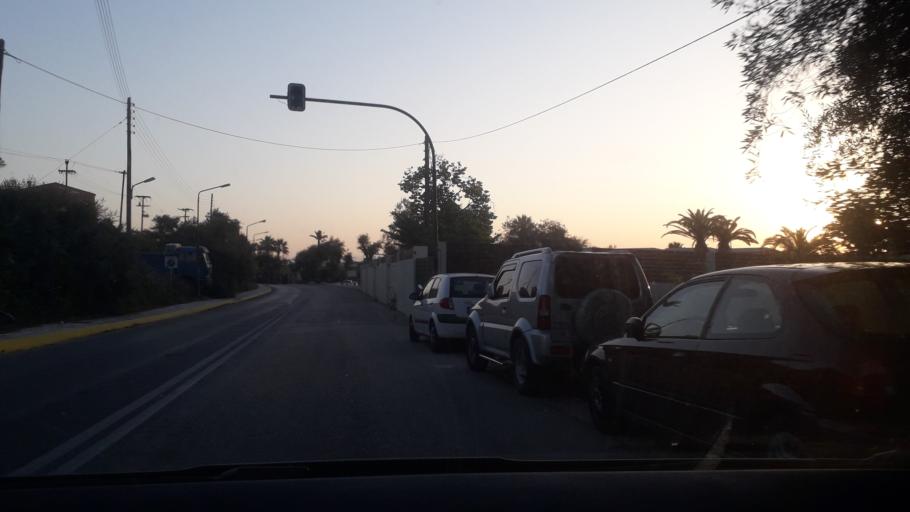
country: GR
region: Ionian Islands
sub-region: Nomos Kerkyras
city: Agios Matthaios
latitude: 39.4883
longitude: 19.9262
